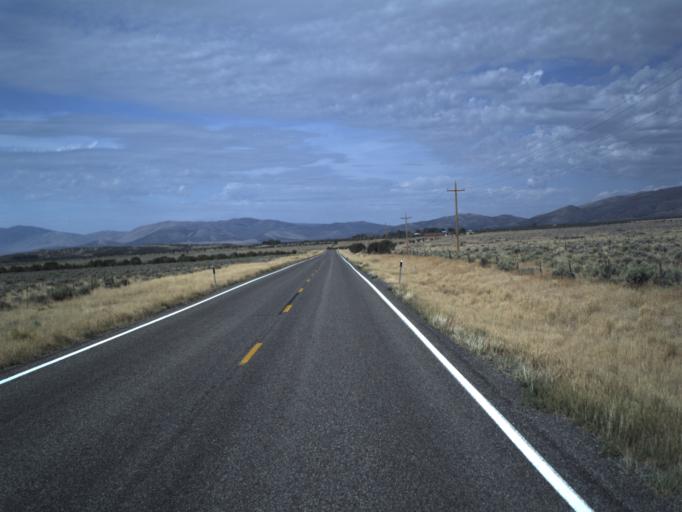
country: US
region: Idaho
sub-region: Cassia County
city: Burley
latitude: 41.8165
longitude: -113.3752
